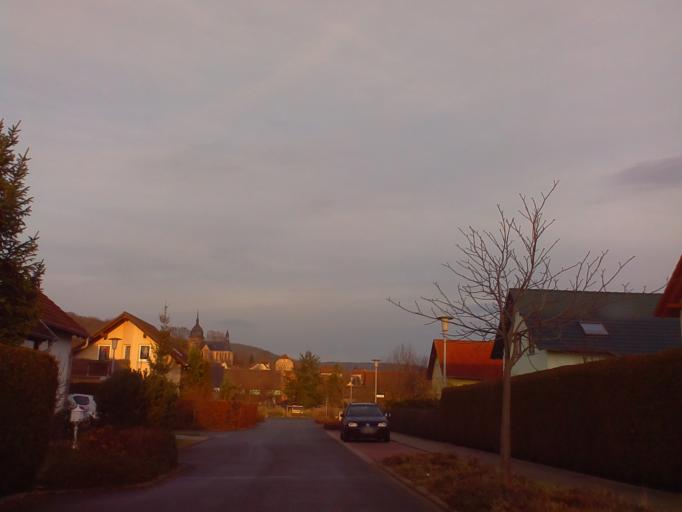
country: DE
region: Thuringia
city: Rothenstein
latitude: 50.8445
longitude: 11.6071
